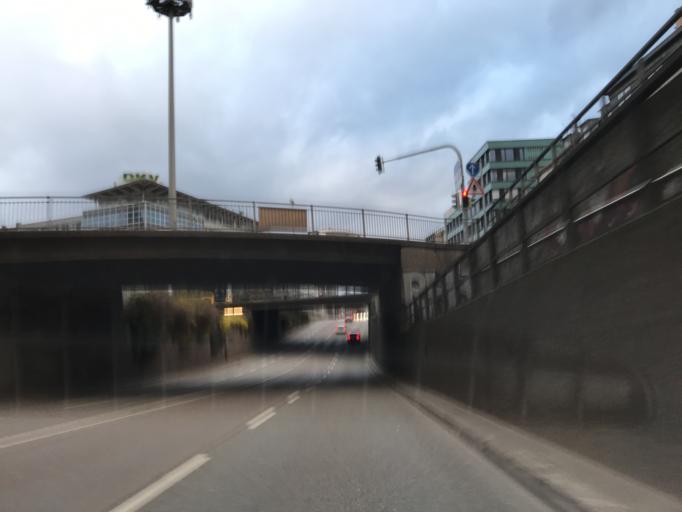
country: DE
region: Baden-Wuerttemberg
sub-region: Regierungsbezirk Stuttgart
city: Stuttgart
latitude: 48.7671
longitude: 9.1733
